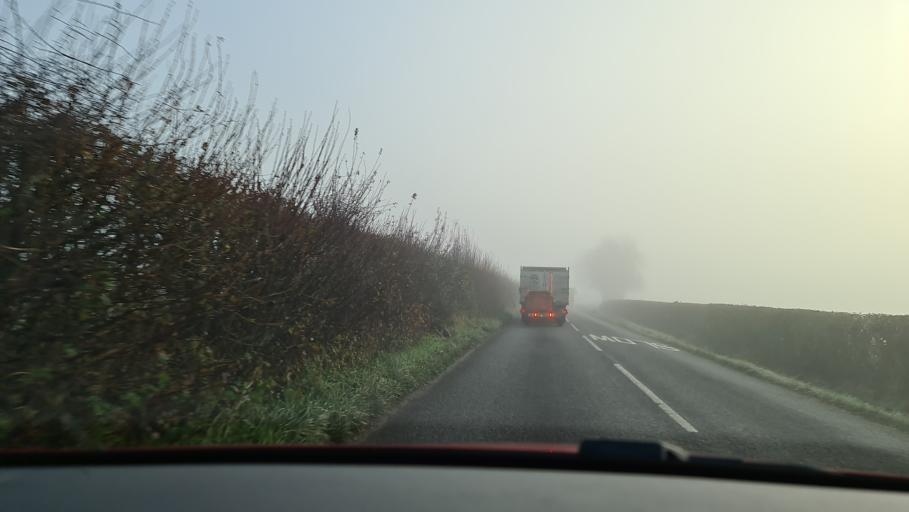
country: GB
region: England
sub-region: Buckinghamshire
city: Aylesbury
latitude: 51.7811
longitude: -0.8183
